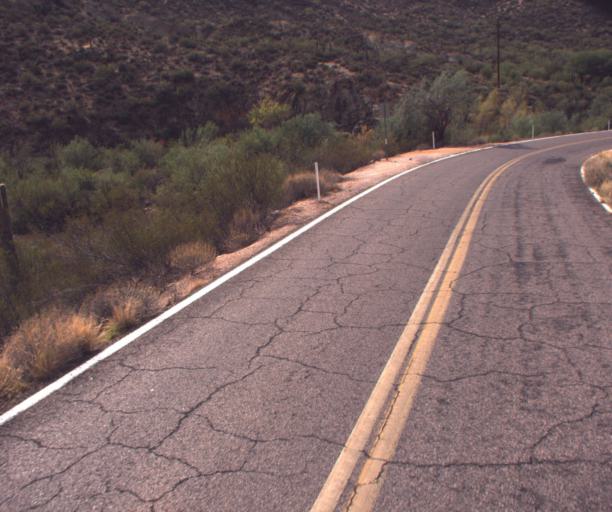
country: US
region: Arizona
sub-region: Pinal County
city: Apache Junction
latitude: 33.5282
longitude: -111.3870
